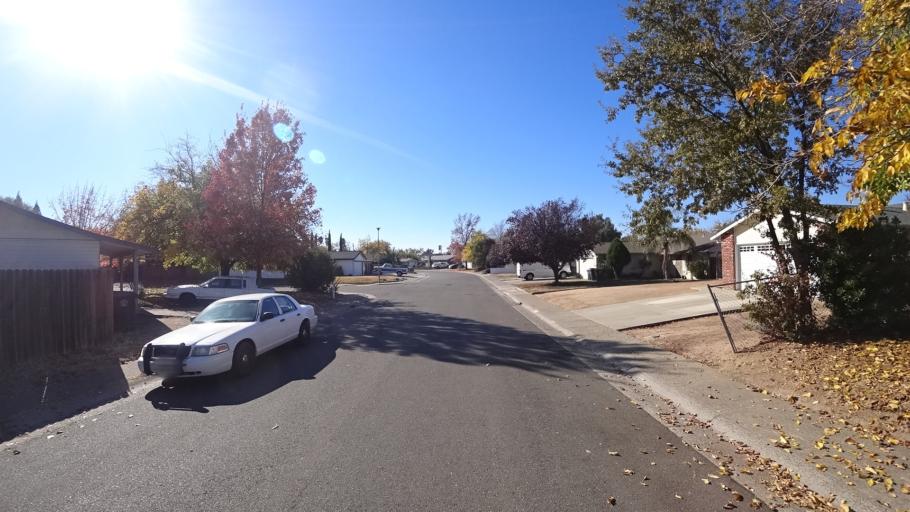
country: US
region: California
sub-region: Sacramento County
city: Antelope
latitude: 38.7161
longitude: -121.3141
